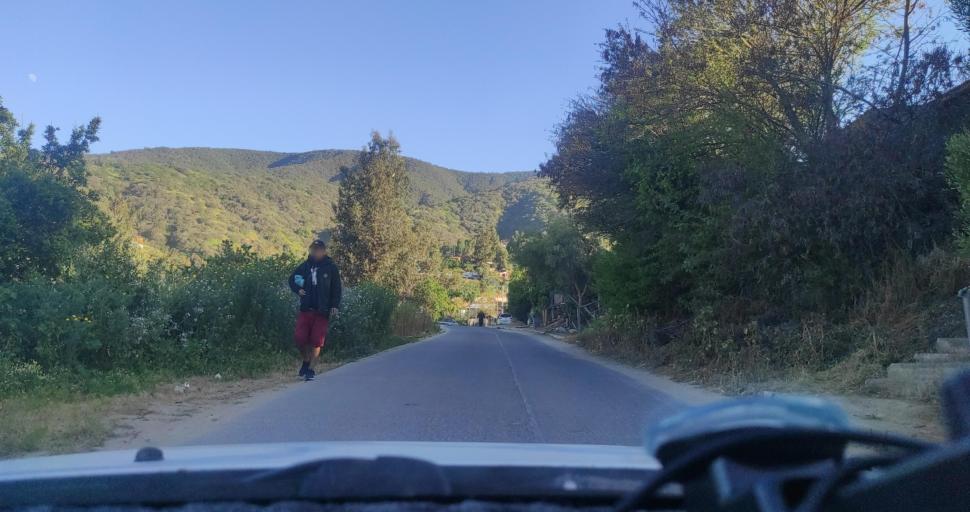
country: CL
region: Valparaiso
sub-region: Provincia de Marga Marga
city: Limache
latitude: -32.9899
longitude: -71.2356
